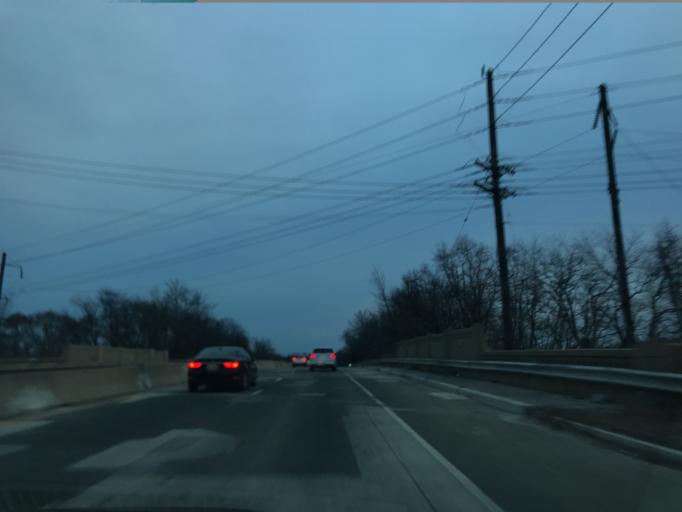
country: US
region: New Jersey
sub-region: Middlesex County
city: Dayton
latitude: 40.3663
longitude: -74.4986
